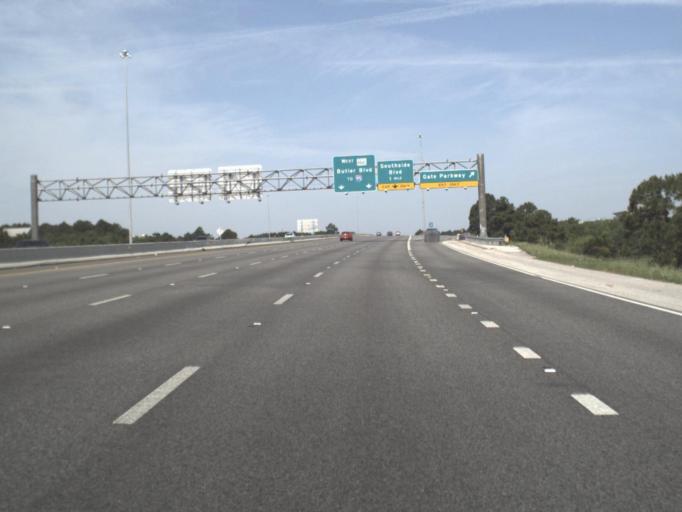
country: US
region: Florida
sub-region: Duval County
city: Jacksonville Beach
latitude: 30.2505
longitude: -81.5299
